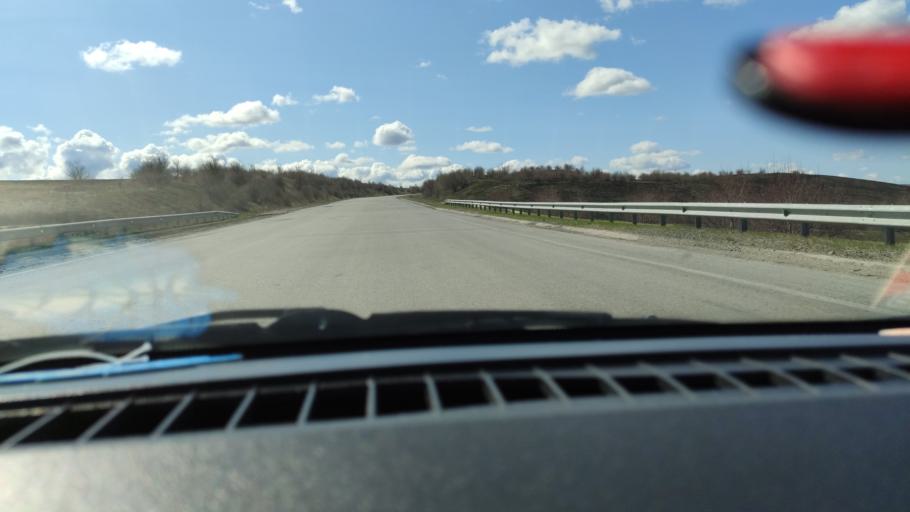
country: RU
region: Samara
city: Varlamovo
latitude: 53.0654
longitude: 48.3539
